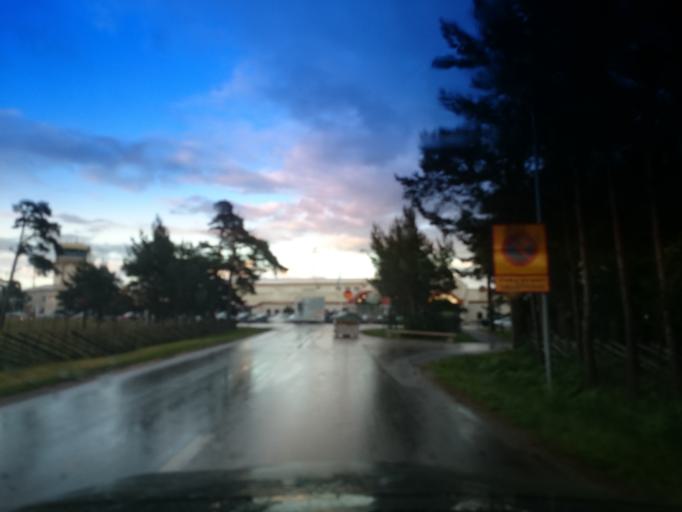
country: SE
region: Gotland
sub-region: Gotland
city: Visby
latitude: 57.6606
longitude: 18.3366
